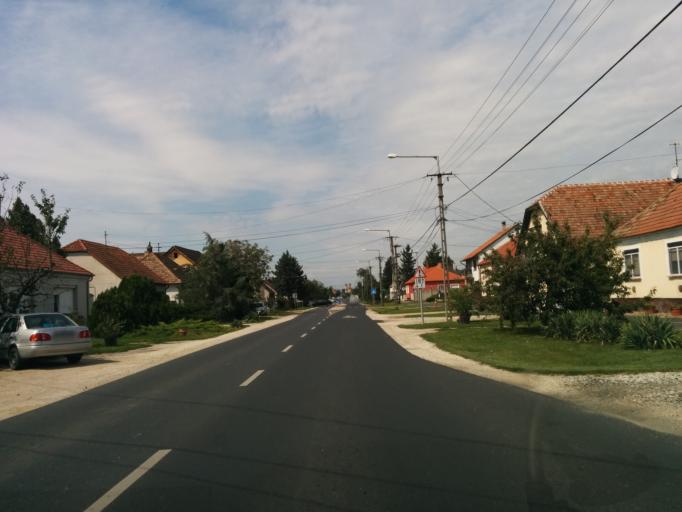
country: HU
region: Gyor-Moson-Sopron
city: Fertod
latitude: 47.6188
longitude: 16.8570
